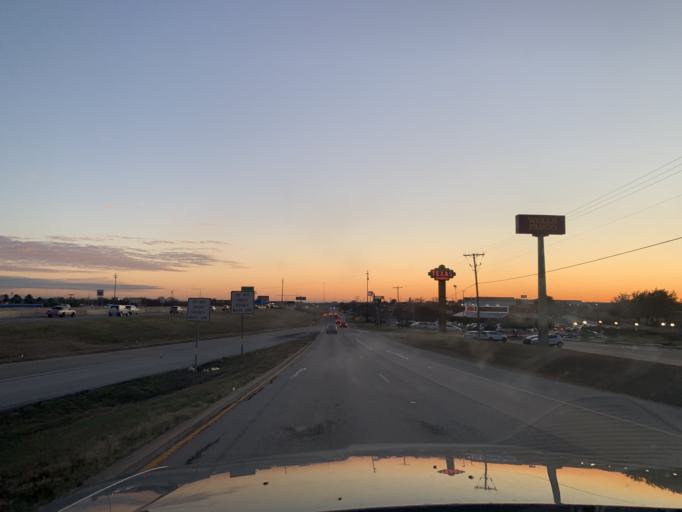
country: US
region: Texas
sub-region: Tarrant County
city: Euless
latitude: 32.8552
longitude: -97.1091
